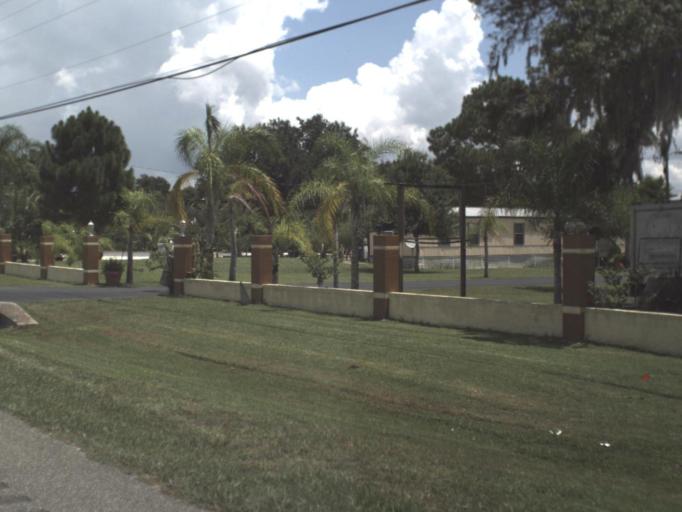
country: US
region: Florida
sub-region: Hillsborough County
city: Sun City Center
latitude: 27.6821
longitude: -82.3459
